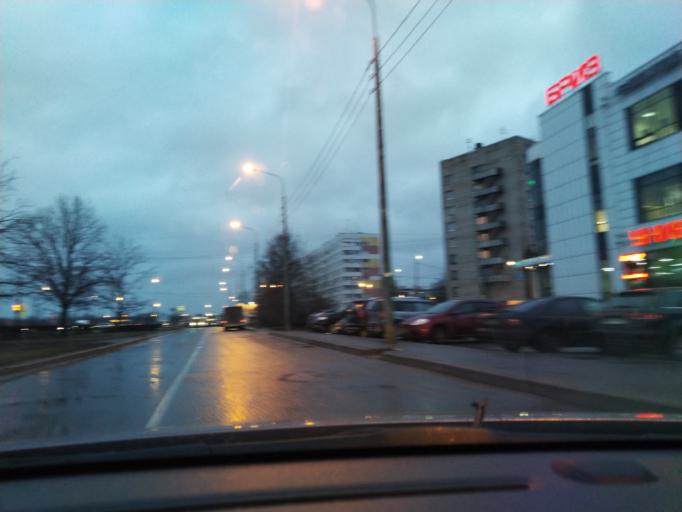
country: RU
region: St.-Petersburg
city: Uritsk
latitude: 59.8276
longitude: 30.1896
